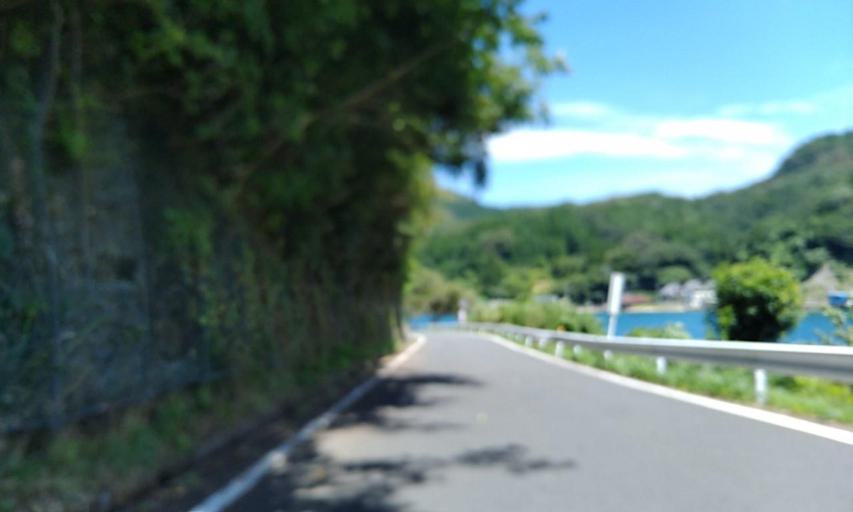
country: JP
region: Kyoto
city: Miyazu
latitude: 35.6686
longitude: 135.2751
